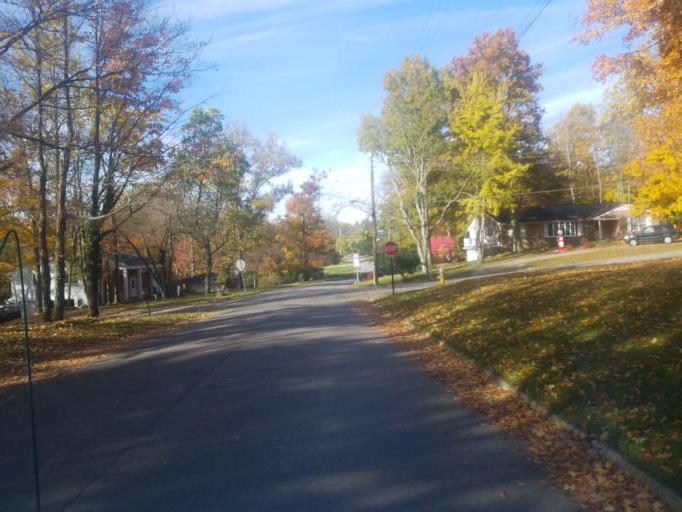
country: US
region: Ohio
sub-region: Richland County
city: Mansfield
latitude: 40.7261
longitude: -82.5223
